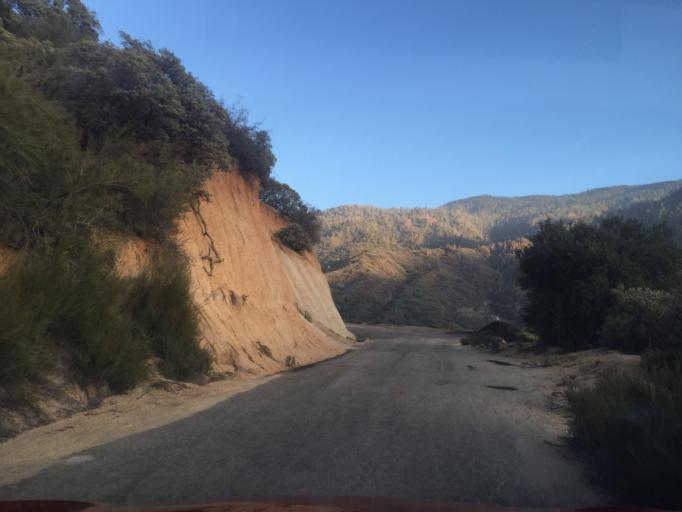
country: US
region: California
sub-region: Tulare County
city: Three Rivers
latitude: 36.4307
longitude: -118.7543
